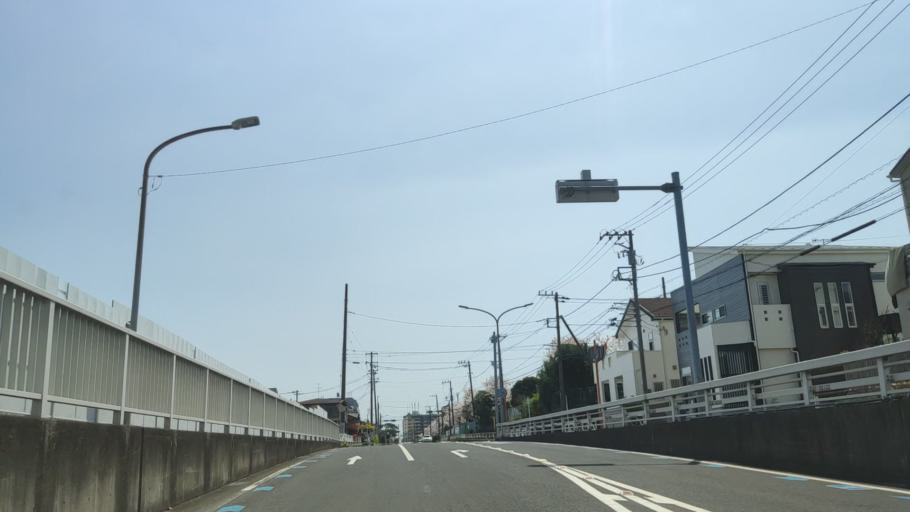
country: JP
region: Kanagawa
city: Hiratsuka
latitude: 35.3240
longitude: 139.3380
